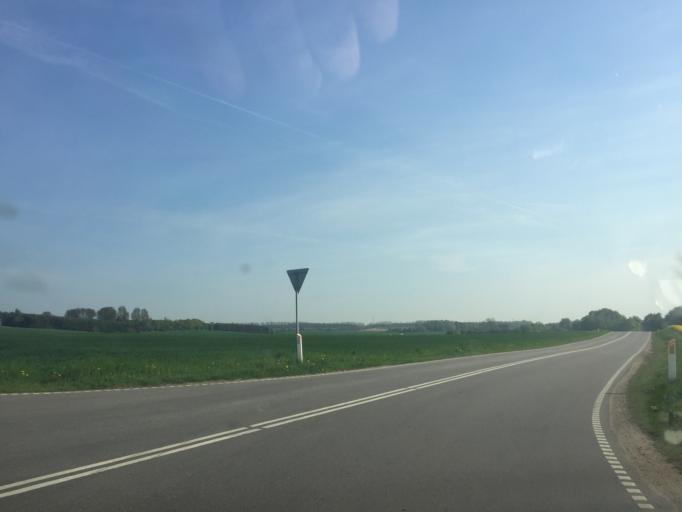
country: DK
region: Capital Region
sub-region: Hoje-Taastrup Kommune
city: Flong
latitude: 55.6727
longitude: 12.2111
